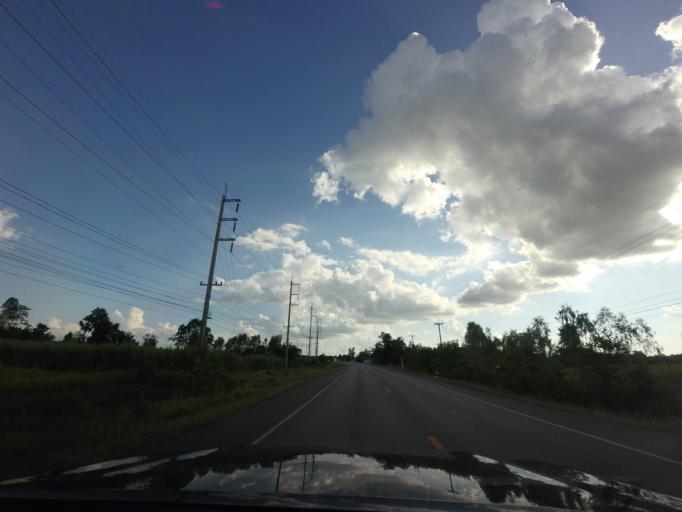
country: TH
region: Changwat Udon Thani
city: Thung Fon
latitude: 17.5160
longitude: 103.2047
